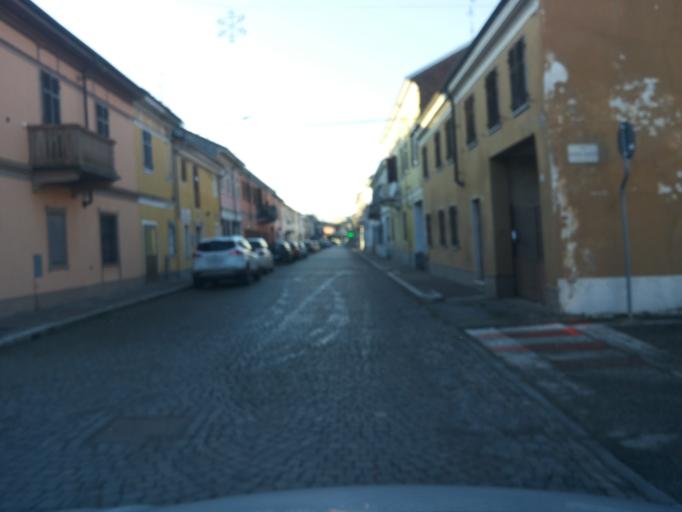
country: IT
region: Piedmont
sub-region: Provincia di Vercelli
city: Lignana
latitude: 45.2857
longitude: 8.3451
